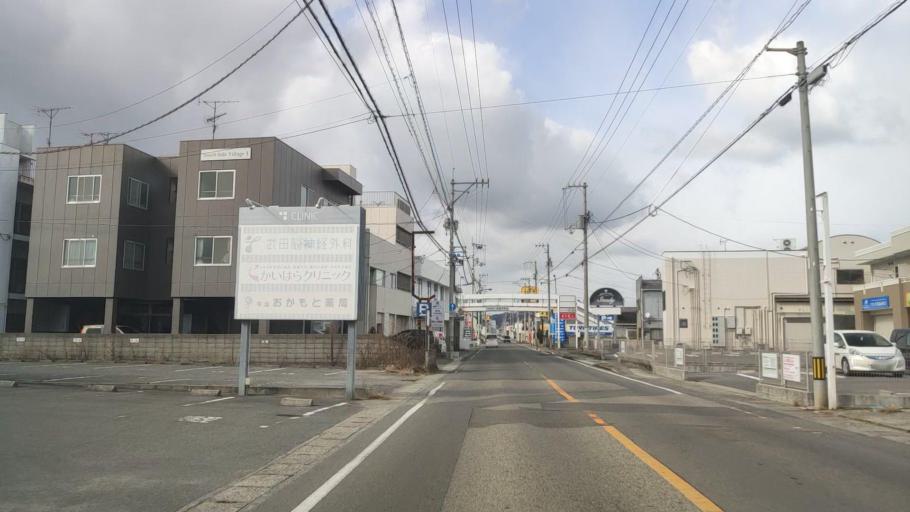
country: JP
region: Ehime
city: Saijo
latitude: 34.0497
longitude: 133.0150
